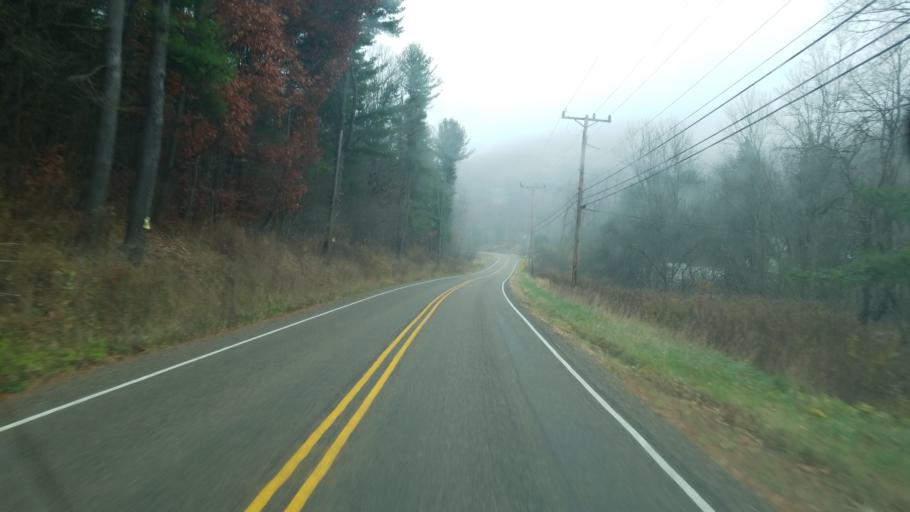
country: US
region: Pennsylvania
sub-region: McKean County
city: Smethport
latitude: 41.8968
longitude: -78.5185
